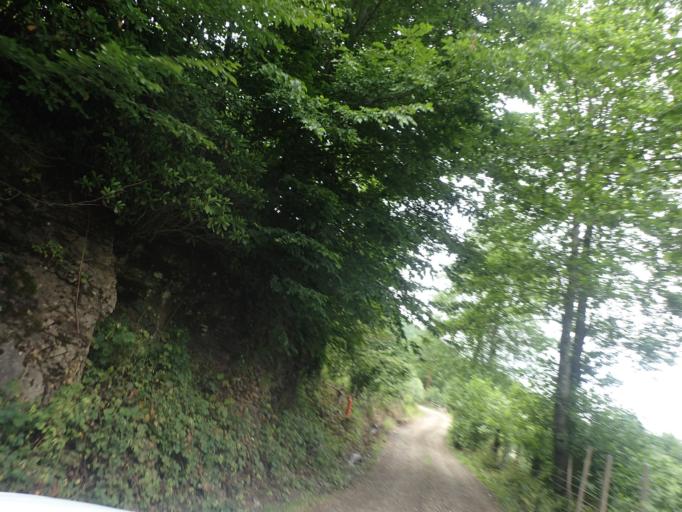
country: TR
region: Samsun
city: Salipazari
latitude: 40.9625
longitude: 36.9272
